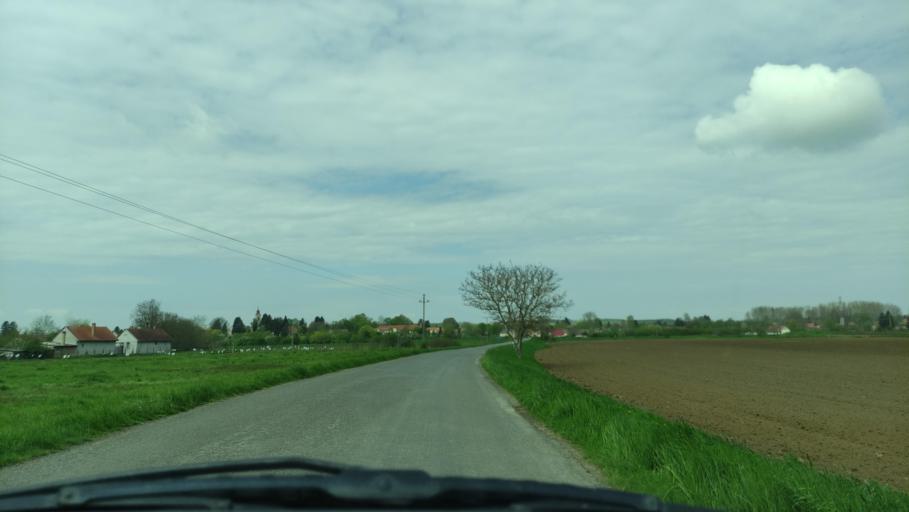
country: HU
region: Baranya
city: Sasd
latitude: 46.3057
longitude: 18.1447
